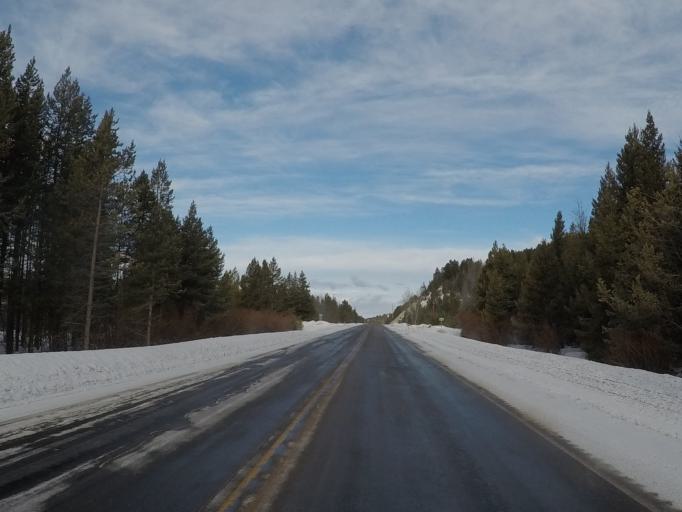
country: US
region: Montana
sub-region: Granite County
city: Philipsburg
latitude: 46.1658
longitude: -113.2059
